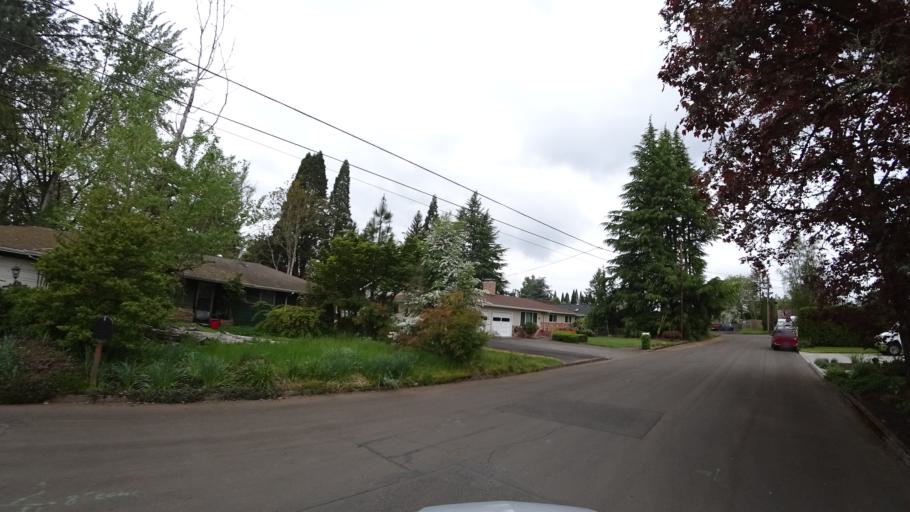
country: US
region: Oregon
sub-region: Washington County
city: Hillsboro
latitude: 45.5319
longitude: -122.9777
